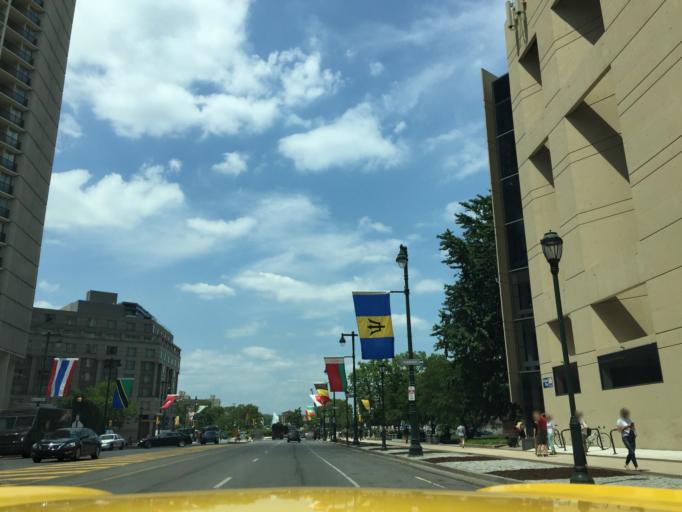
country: US
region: Pennsylvania
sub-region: Philadelphia County
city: Philadelphia
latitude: 39.9562
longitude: -75.1681
